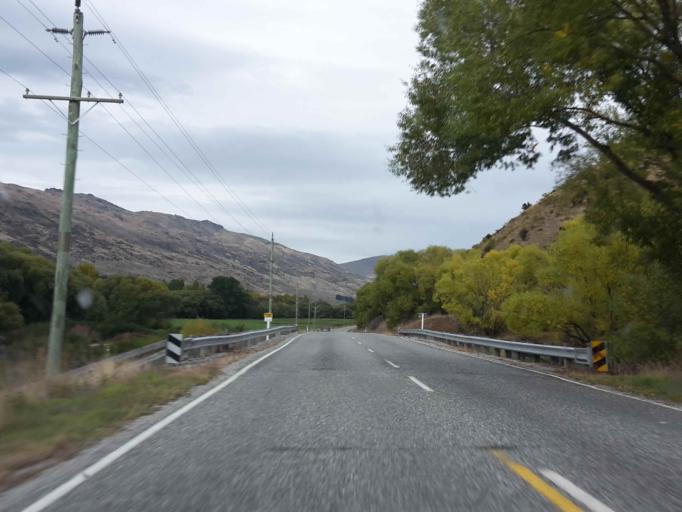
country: NZ
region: Otago
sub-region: Queenstown-Lakes District
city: Wanaka
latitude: -44.8053
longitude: 169.0692
